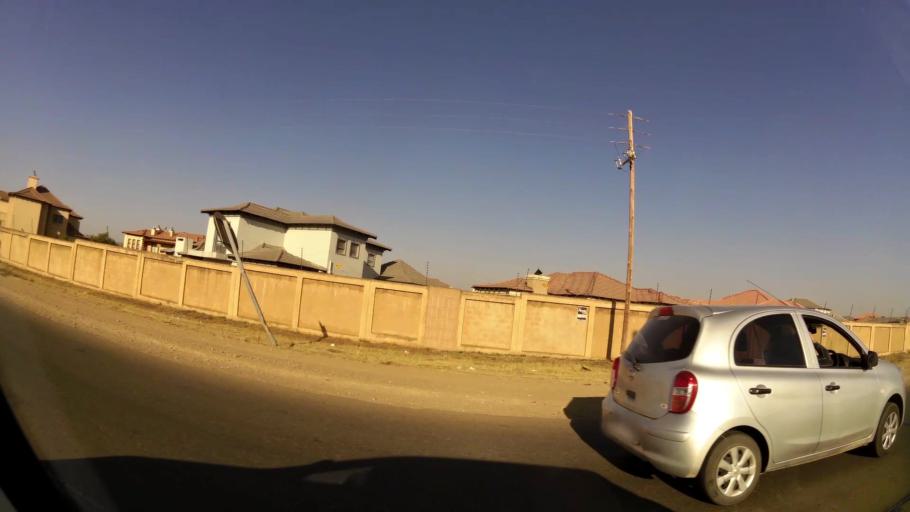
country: ZA
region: Gauteng
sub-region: City of Tshwane Metropolitan Municipality
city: Cullinan
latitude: -25.7533
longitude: 28.3672
